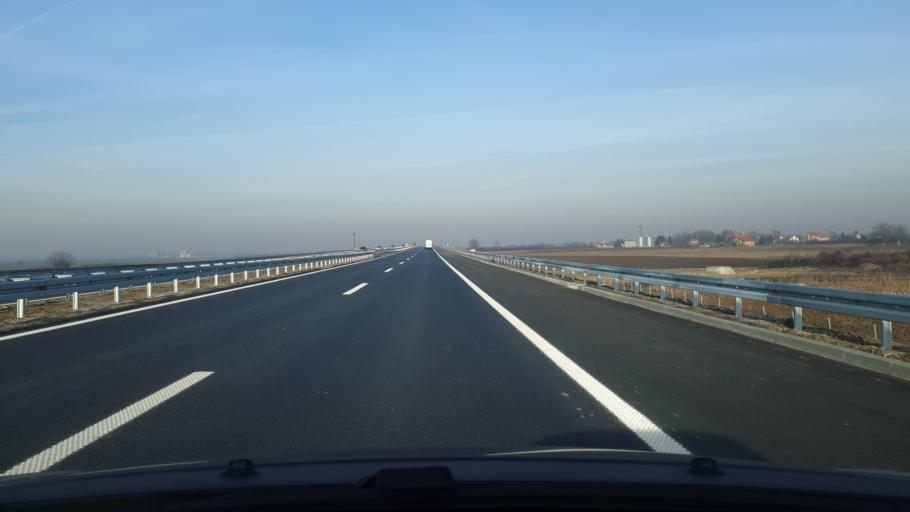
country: RS
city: Boljevci
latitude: 44.7378
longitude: 20.2467
